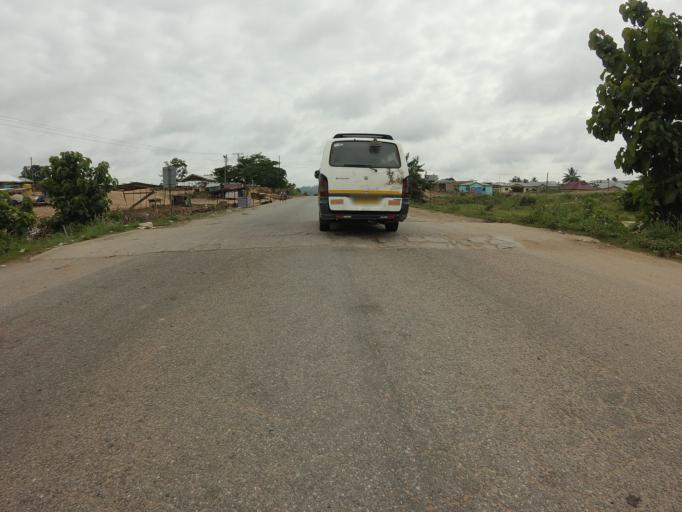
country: GH
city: Bechem
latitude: 7.1231
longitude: -1.7339
